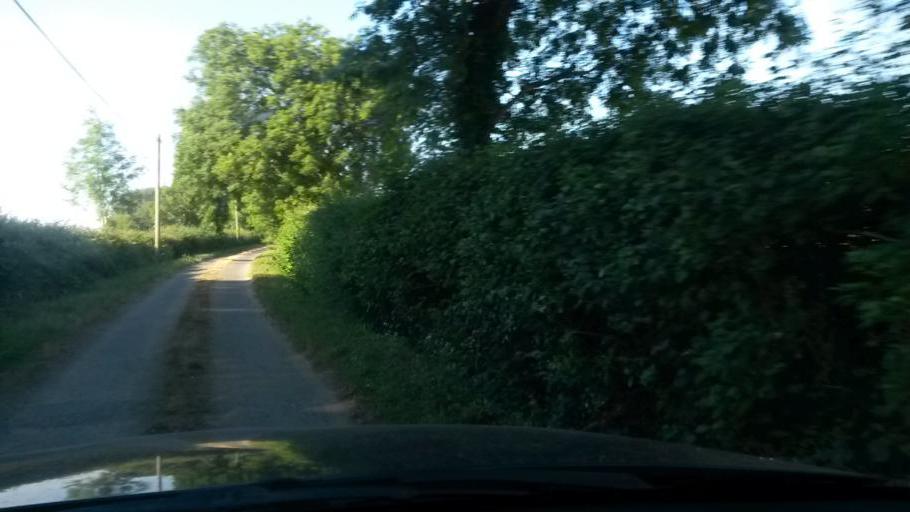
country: IE
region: Leinster
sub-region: Dublin City
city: Finglas
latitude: 53.4381
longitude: -6.3222
